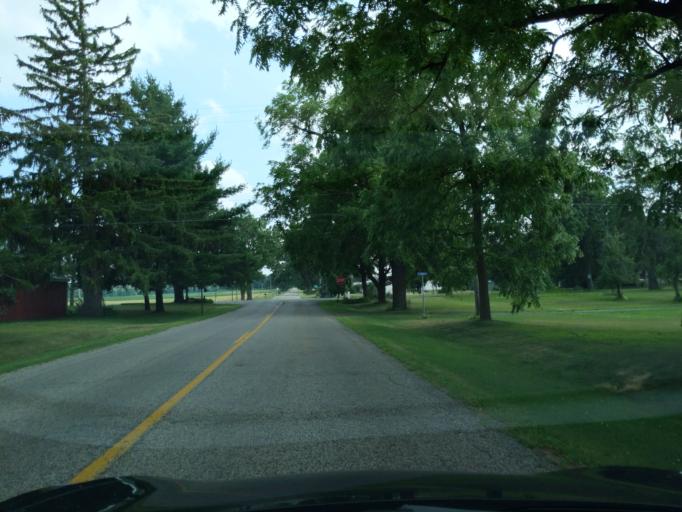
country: US
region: Michigan
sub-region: Eaton County
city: Eaton Rapids
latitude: 42.5101
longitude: -84.6014
